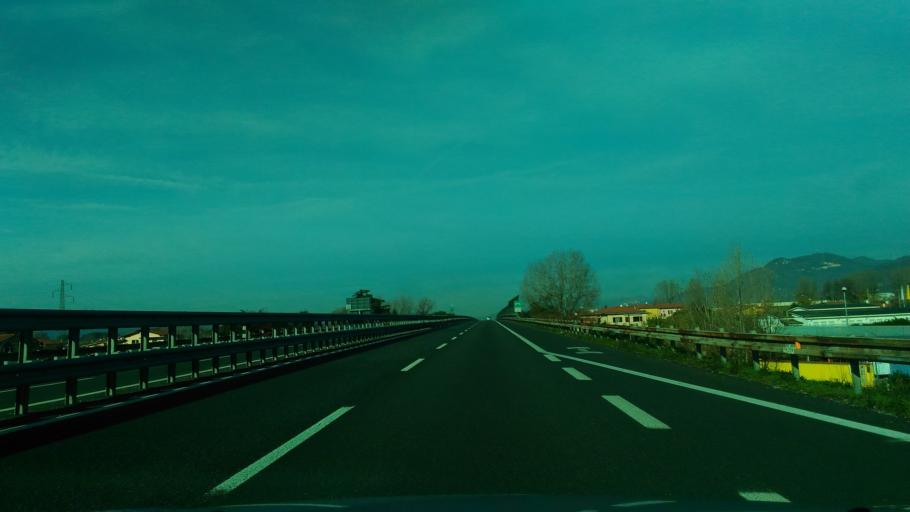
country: IT
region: Tuscany
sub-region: Provincia di Massa-Carrara
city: Massa
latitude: 44.0254
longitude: 10.0969
